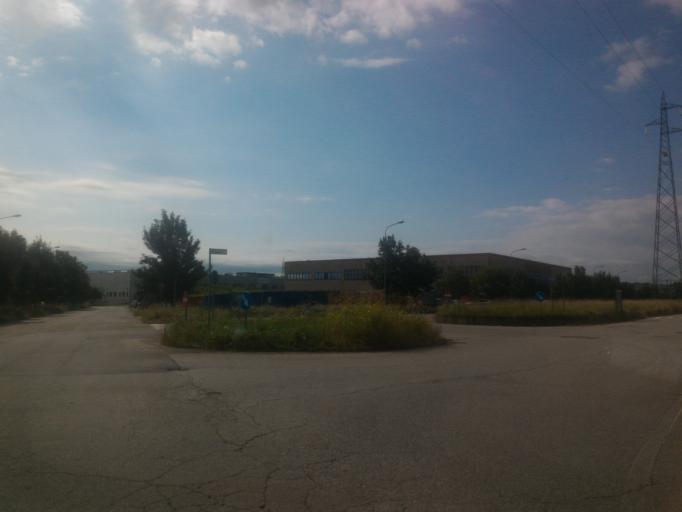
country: IT
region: Piedmont
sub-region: Provincia di Torino
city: Riva
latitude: 44.9012
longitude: 7.3633
